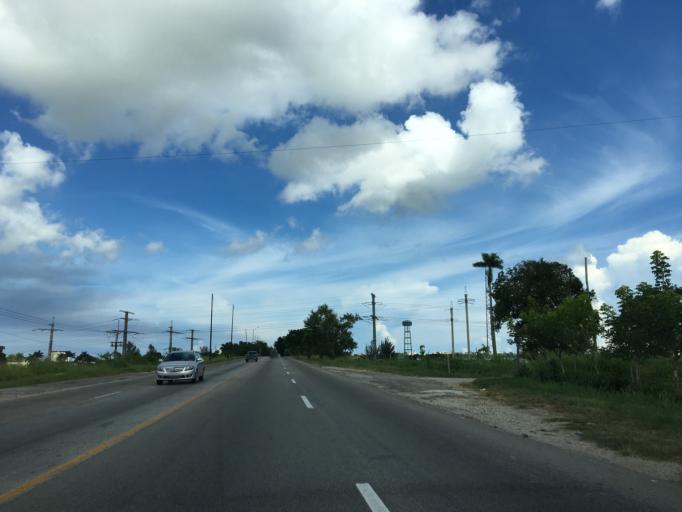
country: CU
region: La Habana
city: Alamar
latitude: 23.1350
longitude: -82.2755
